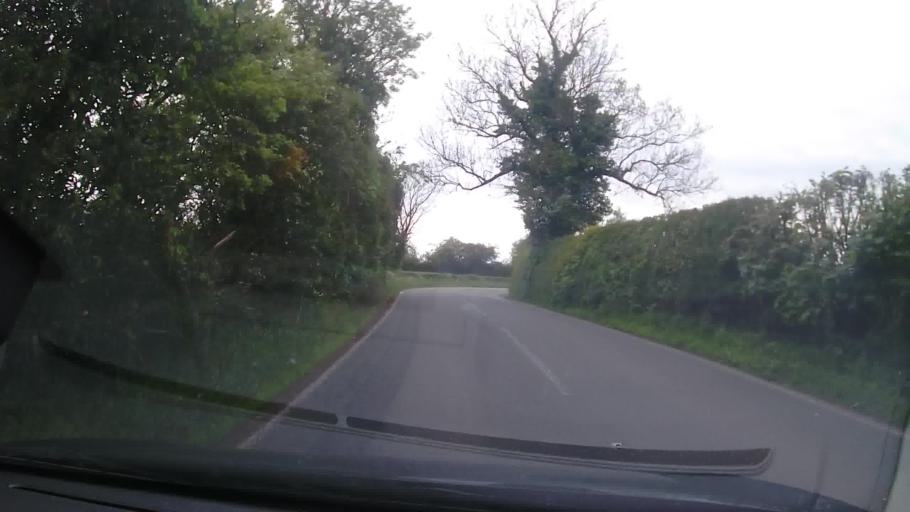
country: GB
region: Wales
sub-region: Wrexham
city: Overton
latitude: 52.9650
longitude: -2.9209
